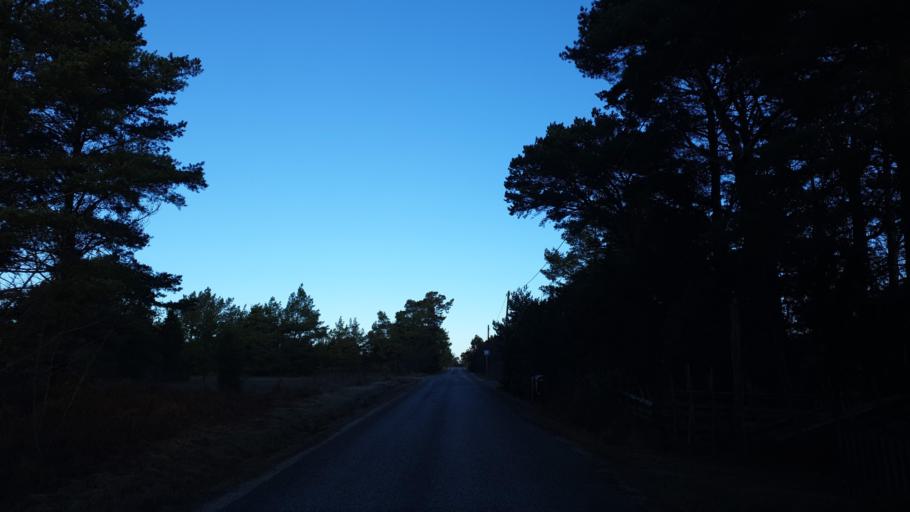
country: SE
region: Gotland
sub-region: Gotland
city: Slite
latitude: 57.3864
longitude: 18.8085
